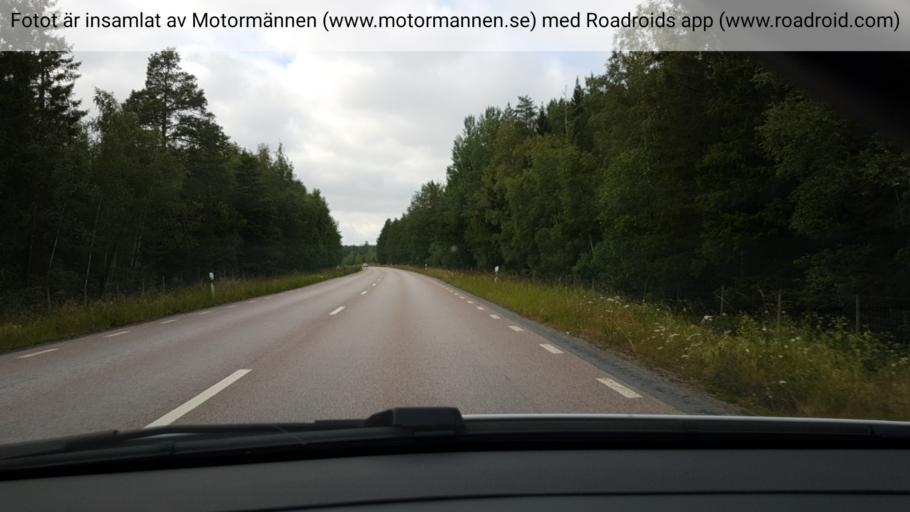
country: SE
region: Uppsala
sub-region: Osthammars Kommun
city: Osterbybruk
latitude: 60.4117
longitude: 17.8660
